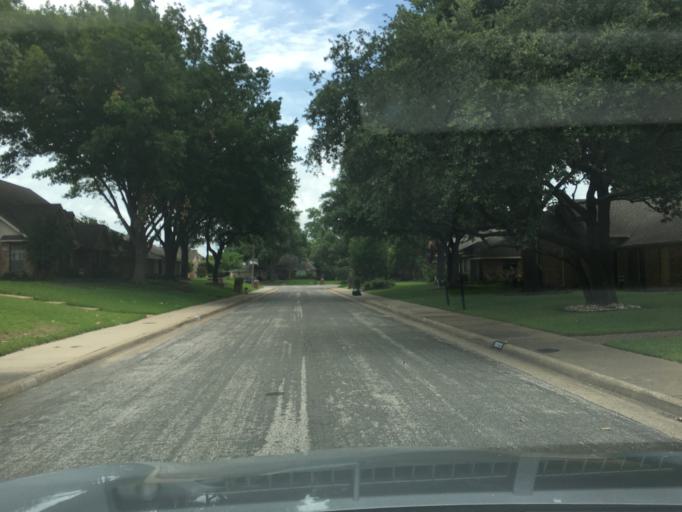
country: US
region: Texas
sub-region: Dallas County
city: Richardson
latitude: 32.9144
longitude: -96.7108
